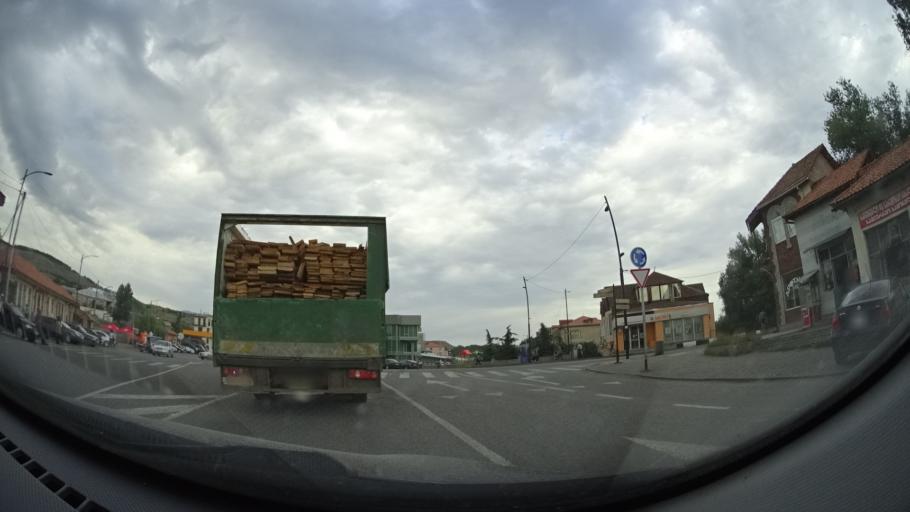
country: GE
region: Samtskhe-Javakheti
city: Akhaltsikhe
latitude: 41.6422
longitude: 42.9814
